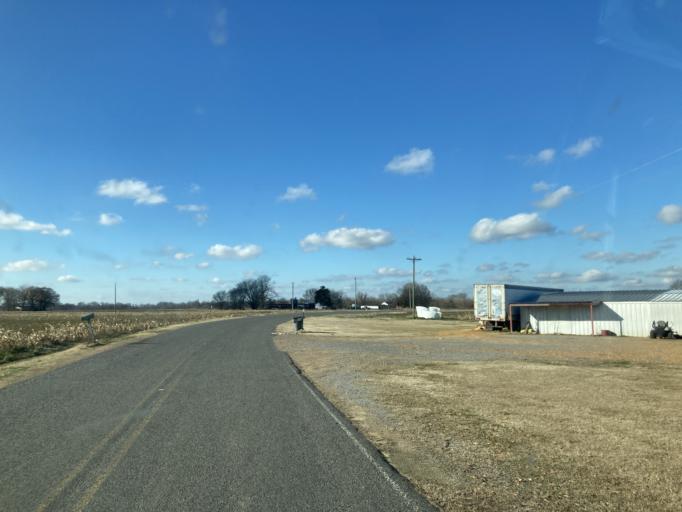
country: US
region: Mississippi
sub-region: Yazoo County
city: Yazoo City
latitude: 32.9267
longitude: -90.4703
